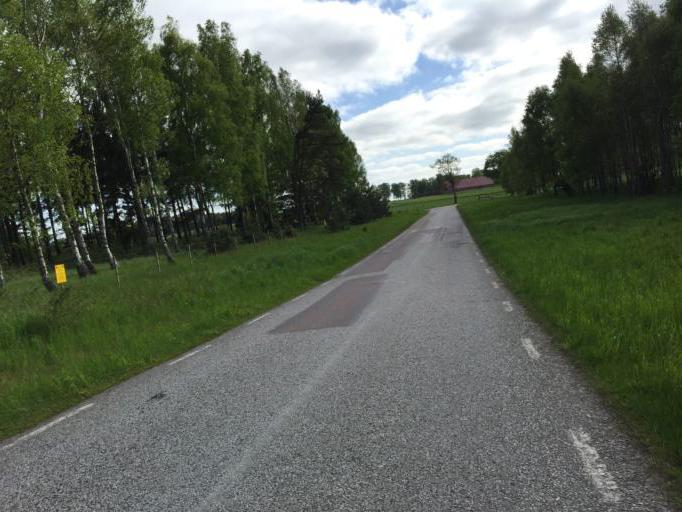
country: SE
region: Skane
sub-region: Sjobo Kommun
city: Blentarp
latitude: 55.6535
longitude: 13.6053
